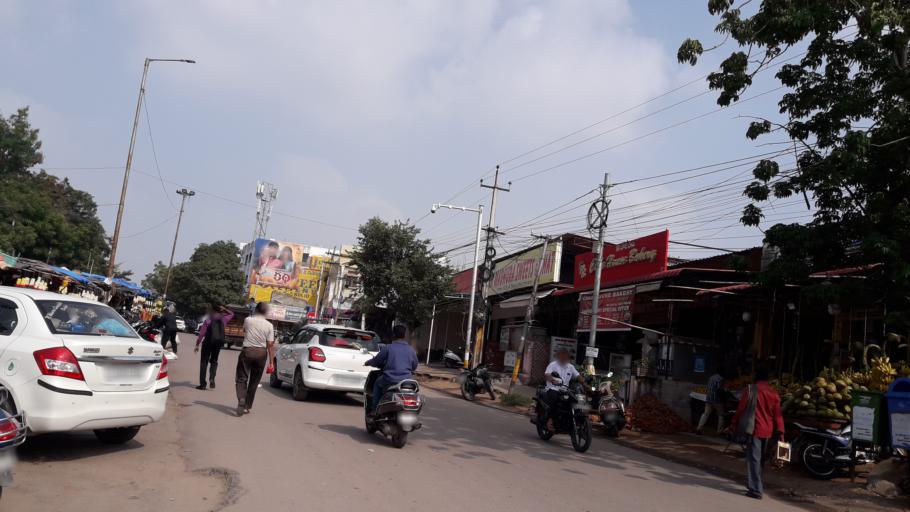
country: IN
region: Telangana
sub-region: Rangareddi
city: Lal Bahadur Nagar
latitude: 17.3306
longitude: 78.5755
